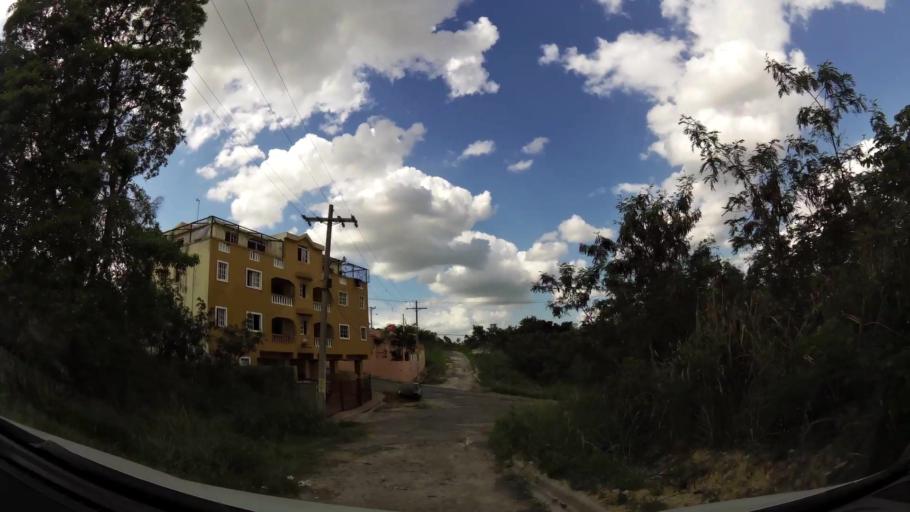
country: DO
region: Nacional
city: Ensanche Luperon
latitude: 18.5301
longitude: -69.8952
